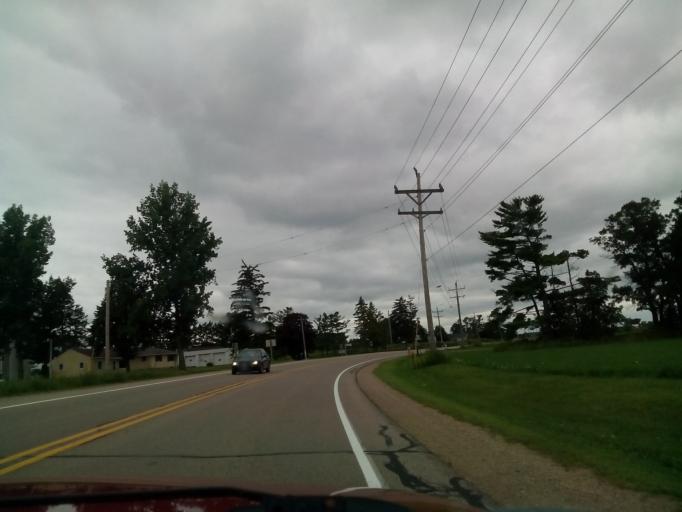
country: US
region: Wisconsin
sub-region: Waupaca County
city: Weyauwega
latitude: 44.2632
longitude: -88.8288
